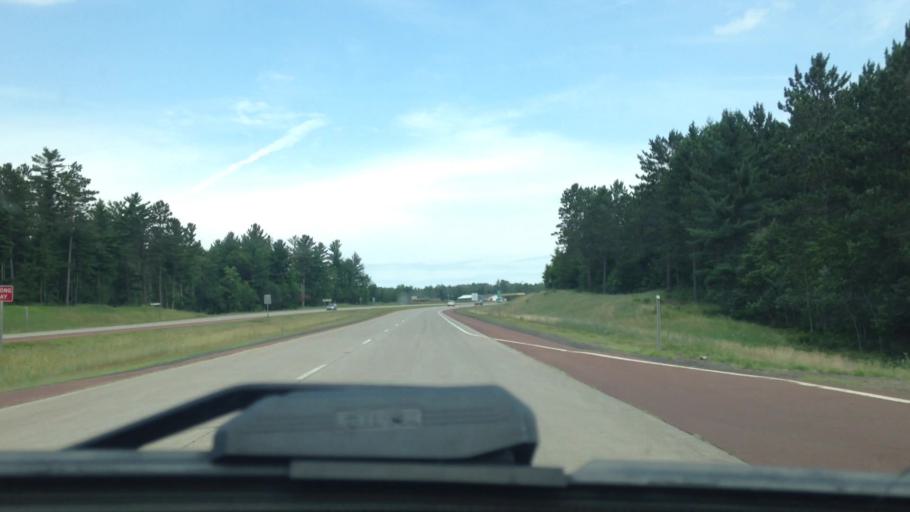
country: US
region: Wisconsin
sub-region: Douglas County
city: Lake Nebagamon
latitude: 46.3456
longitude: -91.8348
